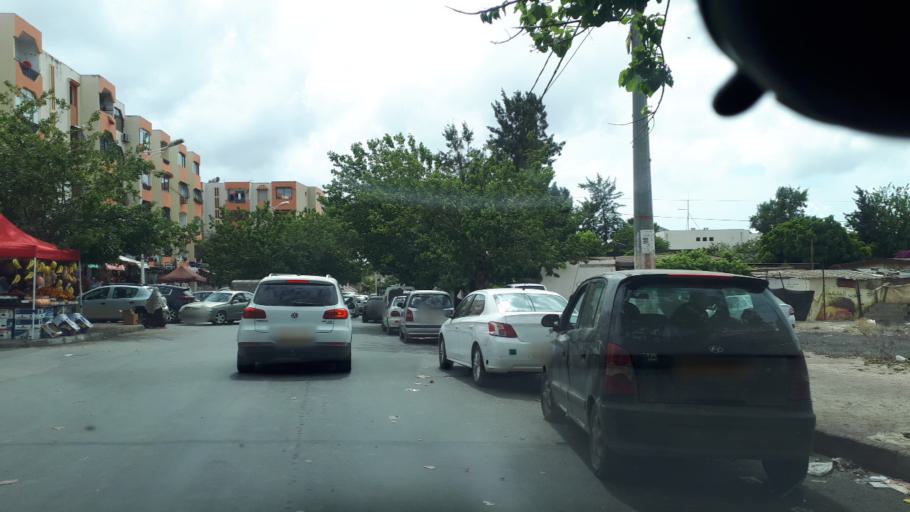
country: DZ
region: Tipaza
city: Cheraga
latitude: 36.7434
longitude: 2.9118
